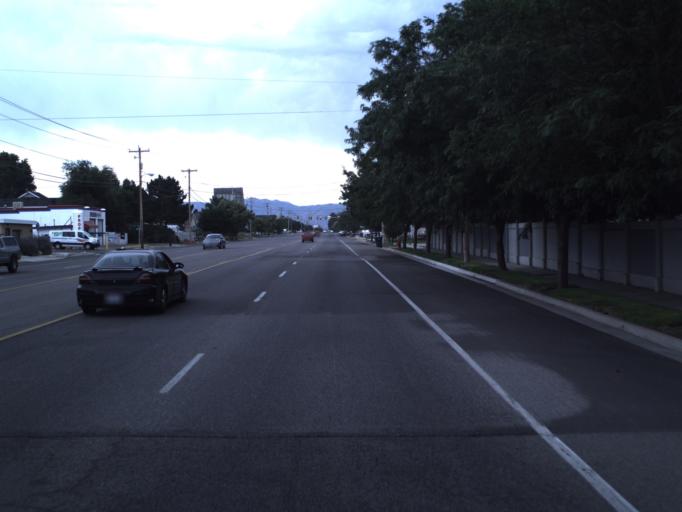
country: US
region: Utah
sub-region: Salt Lake County
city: Sandy City
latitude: 40.5981
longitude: -111.8723
